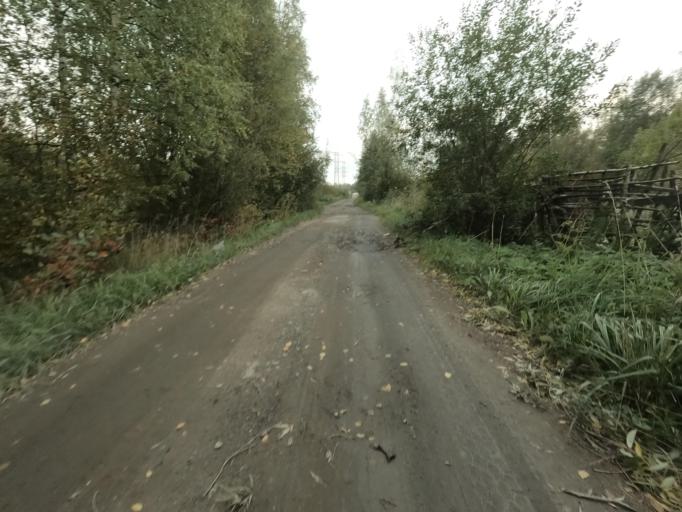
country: RU
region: St.-Petersburg
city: Sapernyy
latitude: 59.7744
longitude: 30.6505
